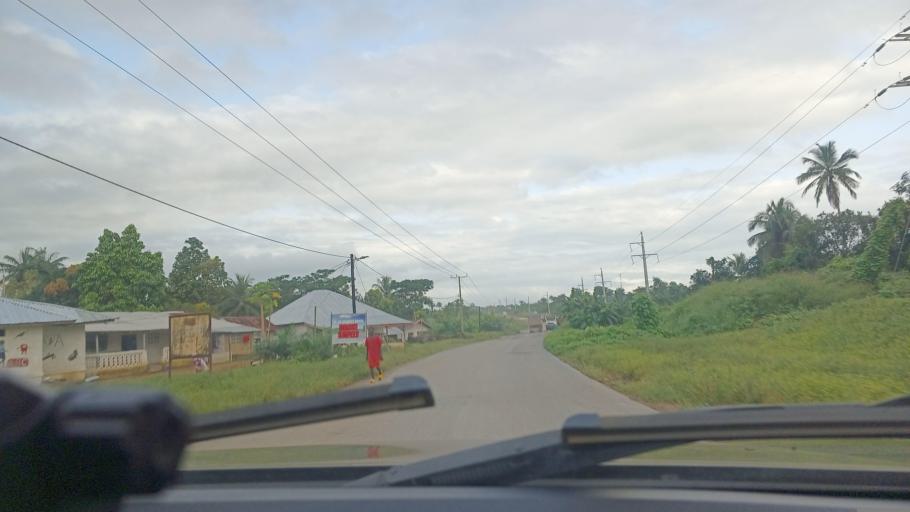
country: LR
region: Montserrado
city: Monrovia
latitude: 6.5725
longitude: -10.8810
